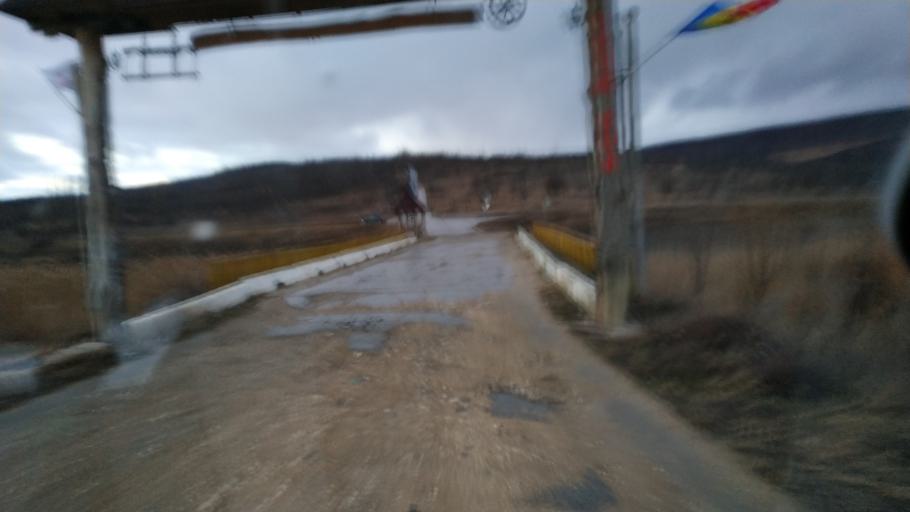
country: MD
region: Taraclia
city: Telenesti
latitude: 47.3938
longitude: 28.3328
